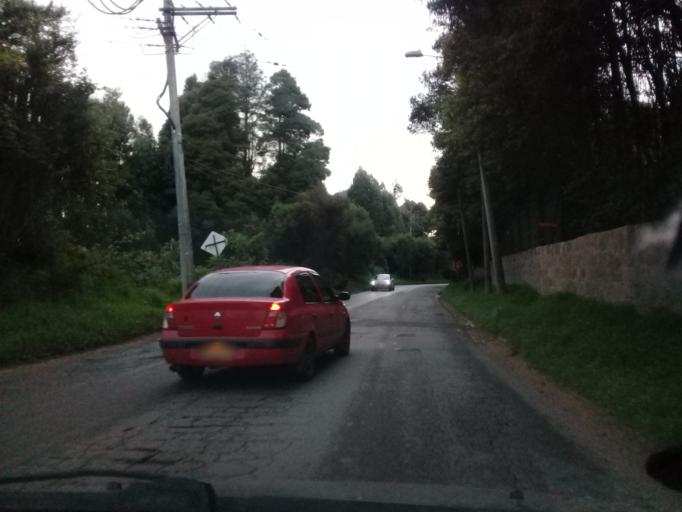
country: CO
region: Cundinamarca
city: Cajica
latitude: 4.9289
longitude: -74.0540
